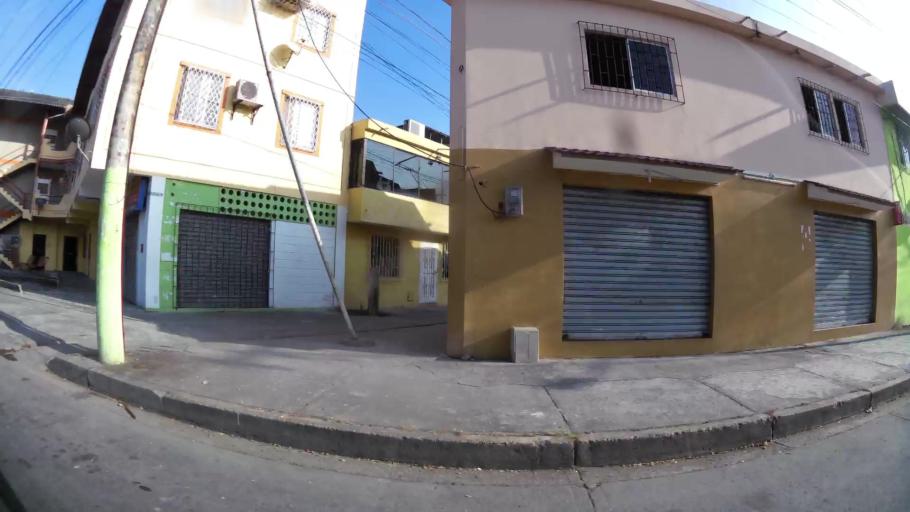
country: EC
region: Guayas
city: Eloy Alfaro
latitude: -2.1873
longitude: -79.8544
